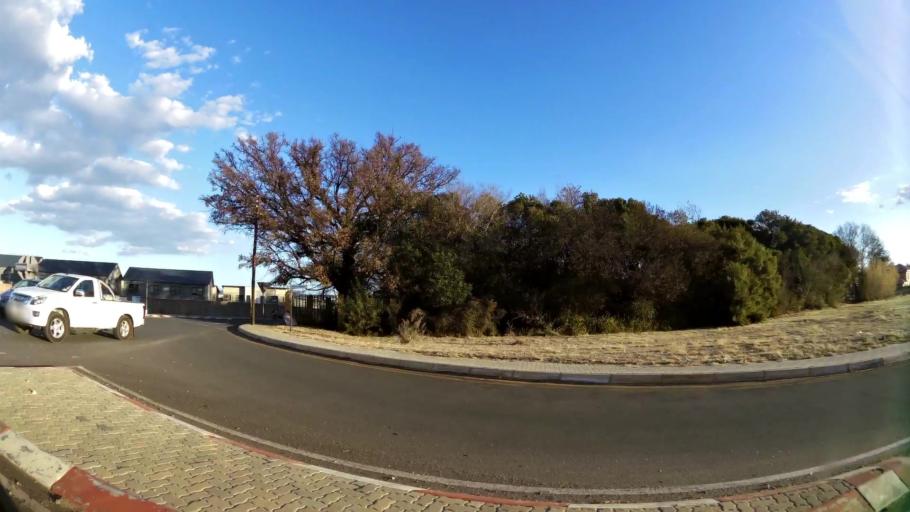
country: ZA
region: North-West
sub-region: Dr Kenneth Kaunda District Municipality
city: Potchefstroom
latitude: -26.6811
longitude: 27.1025
